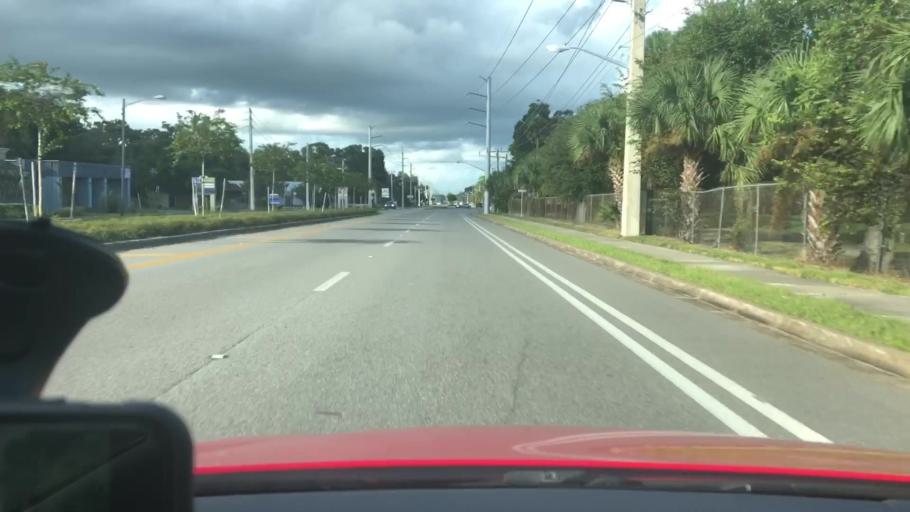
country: US
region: Florida
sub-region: Volusia County
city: South Daytona
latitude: 29.1802
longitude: -81.0168
